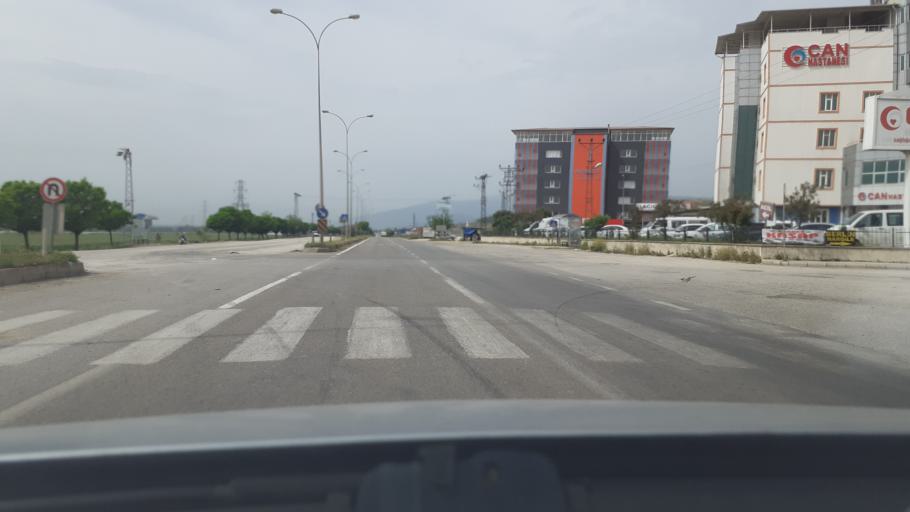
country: TR
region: Hatay
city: Kirikhan
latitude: 36.4799
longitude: 36.3563
